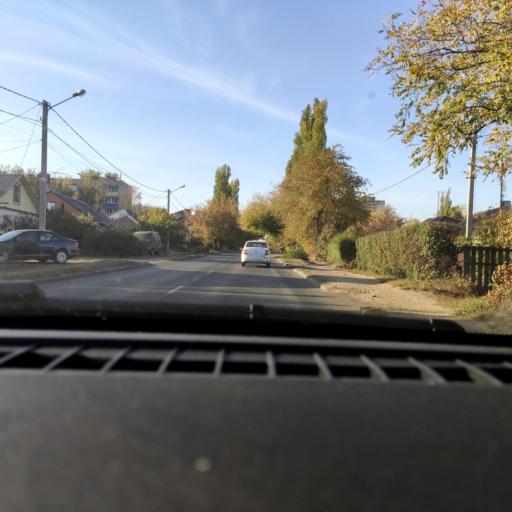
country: RU
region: Voronezj
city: Maslovka
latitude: 51.6211
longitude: 39.2518
